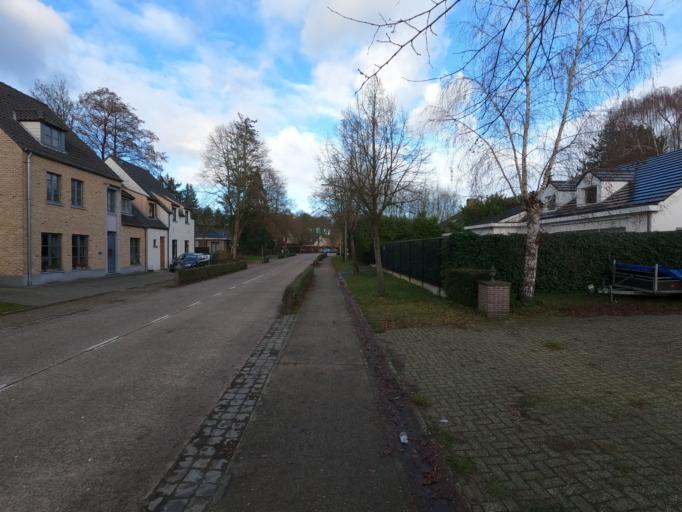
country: BE
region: Flanders
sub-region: Provincie Antwerpen
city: Schilde
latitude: 51.2889
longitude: 4.5690
